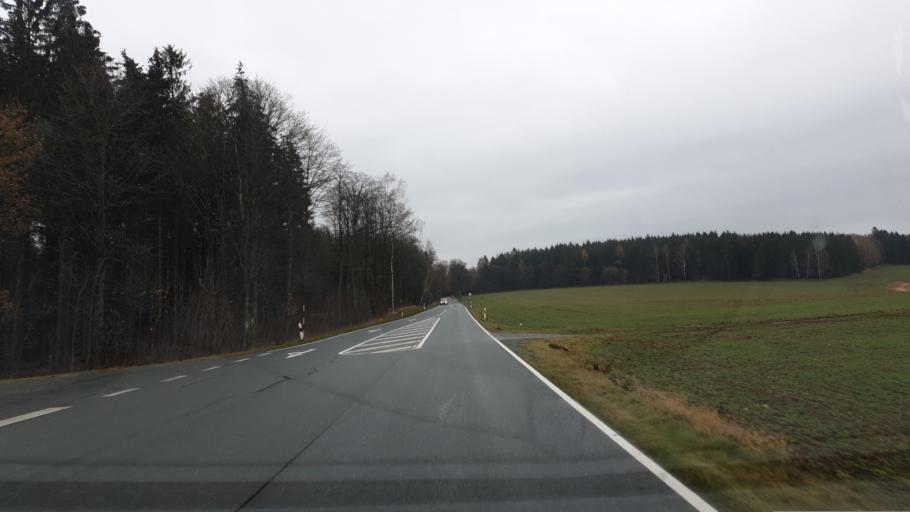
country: DE
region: Saxony
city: Ehrenfriedersdorf
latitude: 50.6321
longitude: 12.9813
